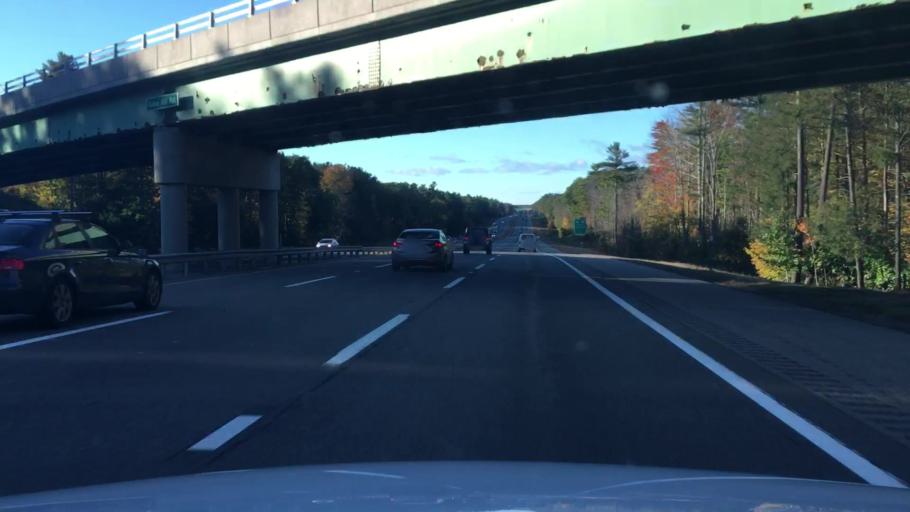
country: US
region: Maine
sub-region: York County
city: Wells Beach Station
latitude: 43.3574
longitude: -70.5893
